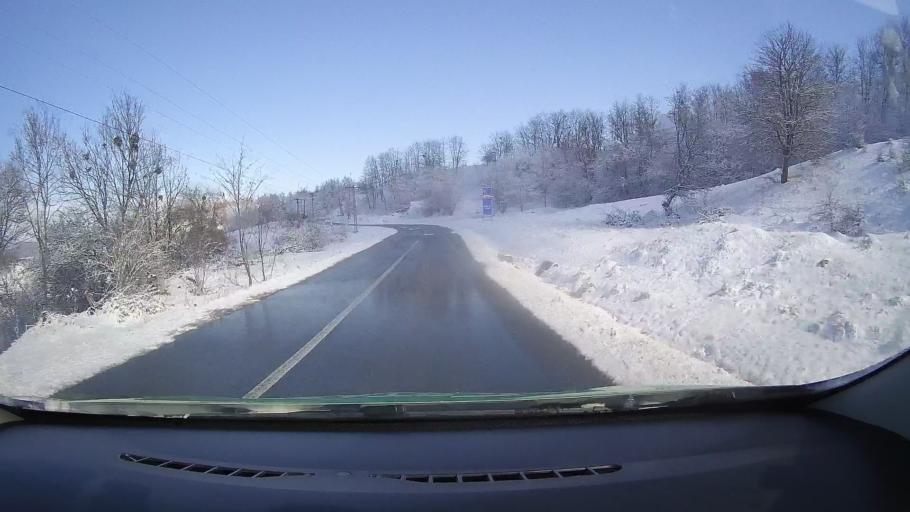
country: RO
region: Sibiu
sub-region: Comuna Rosia
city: Rosia
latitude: 45.7885
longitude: 24.3741
